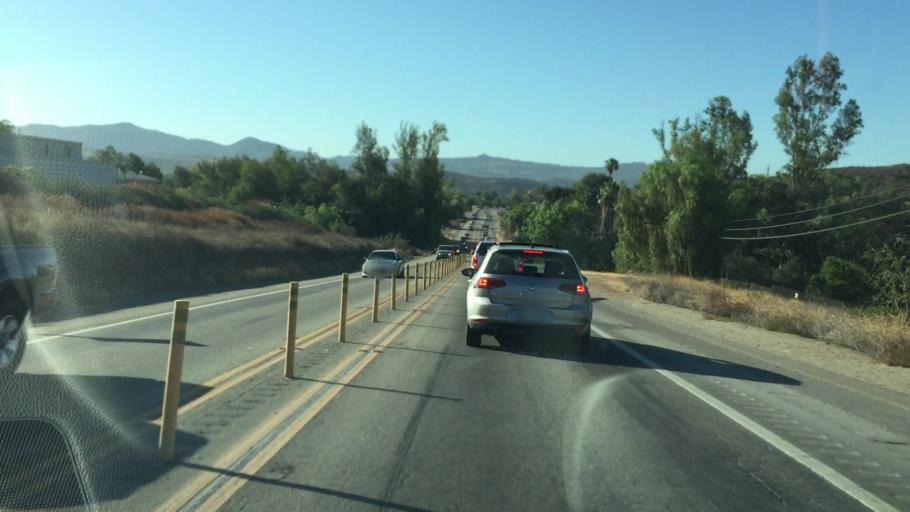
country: US
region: California
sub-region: San Diego County
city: Eucalyptus Hills
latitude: 32.8852
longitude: -116.9316
